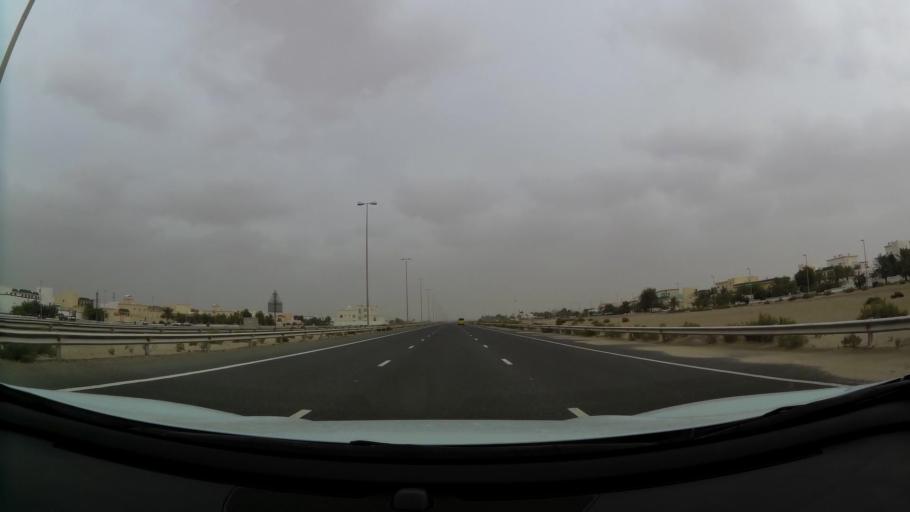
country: AE
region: Abu Dhabi
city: Abu Dhabi
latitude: 24.3680
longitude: 54.6621
